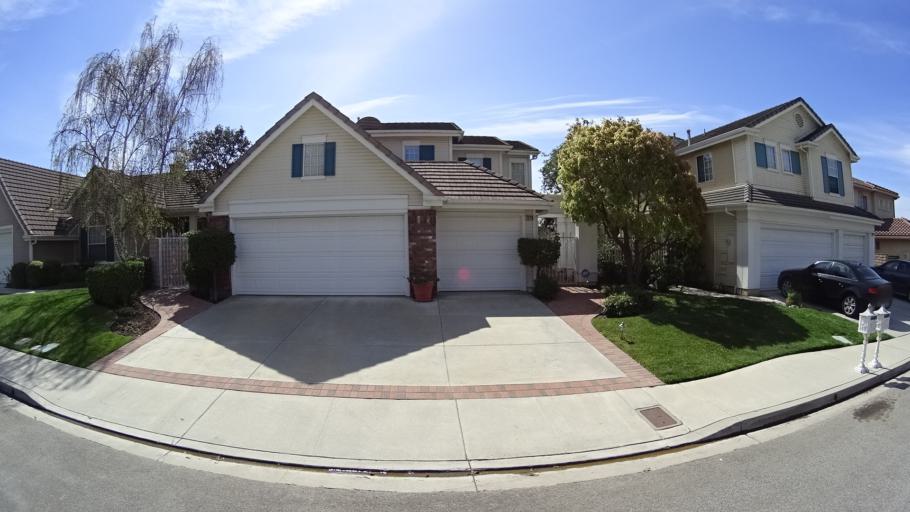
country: US
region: California
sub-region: Ventura County
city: Thousand Oaks
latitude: 34.2214
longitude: -118.8359
